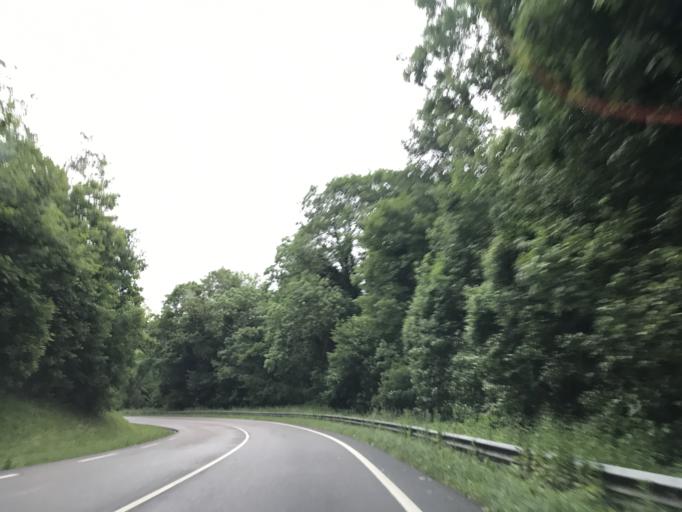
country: FR
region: Ile-de-France
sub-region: Departement des Yvelines
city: Bennecourt
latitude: 49.0285
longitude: 1.5490
